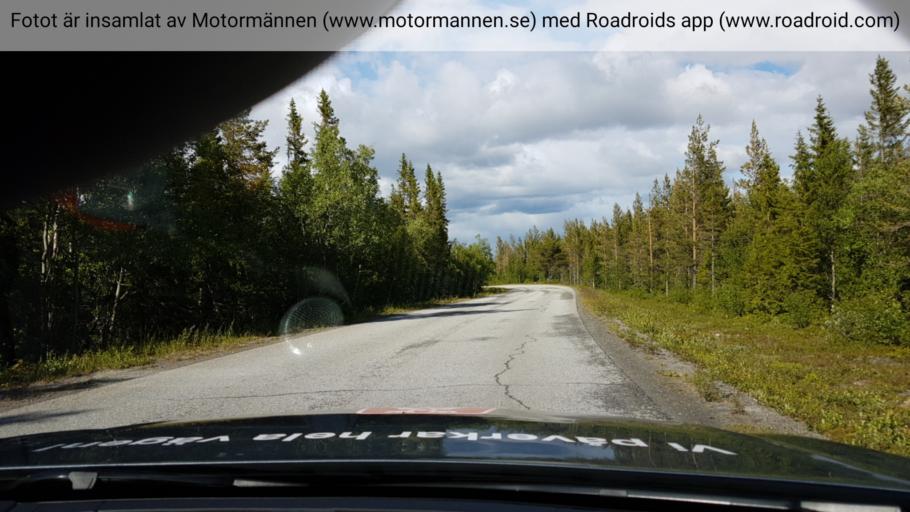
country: SE
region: Jaemtland
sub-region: Krokoms Kommun
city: Valla
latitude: 63.0333
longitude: 13.9518
